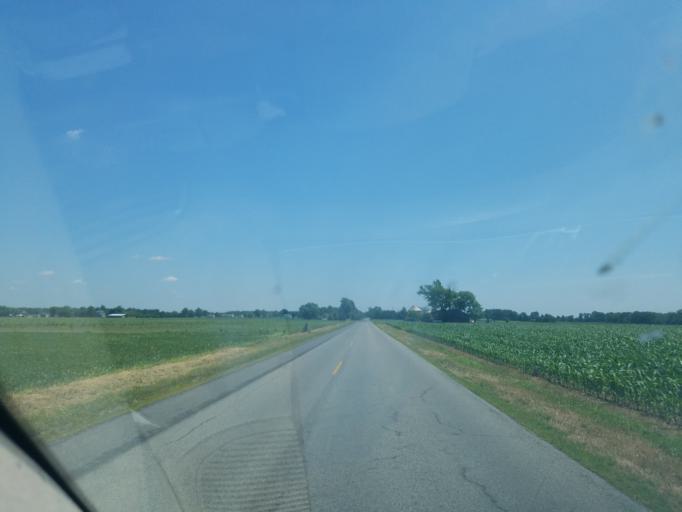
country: US
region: Ohio
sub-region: Allen County
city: Elida
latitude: 40.7873
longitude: -84.2546
